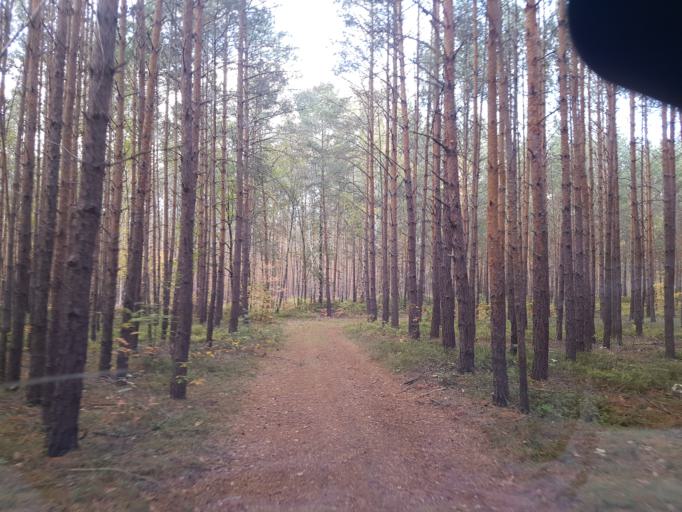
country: DE
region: Brandenburg
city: Finsterwalde
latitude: 51.5727
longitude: 13.6951
